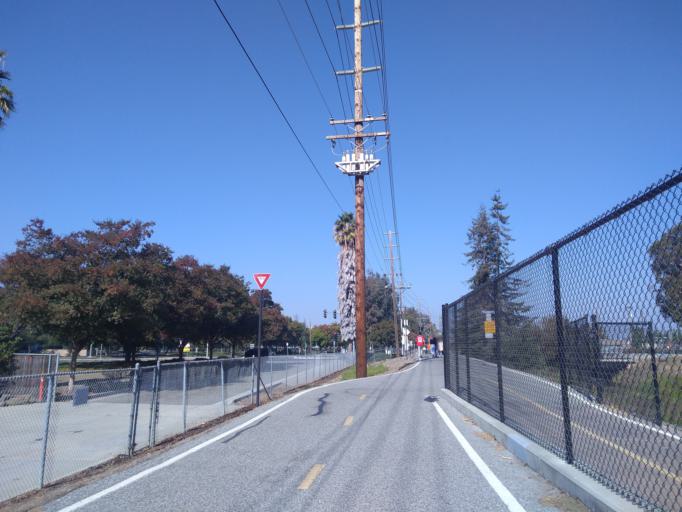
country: US
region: California
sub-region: Santa Clara County
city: Santa Clara
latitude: 37.3897
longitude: -121.9688
